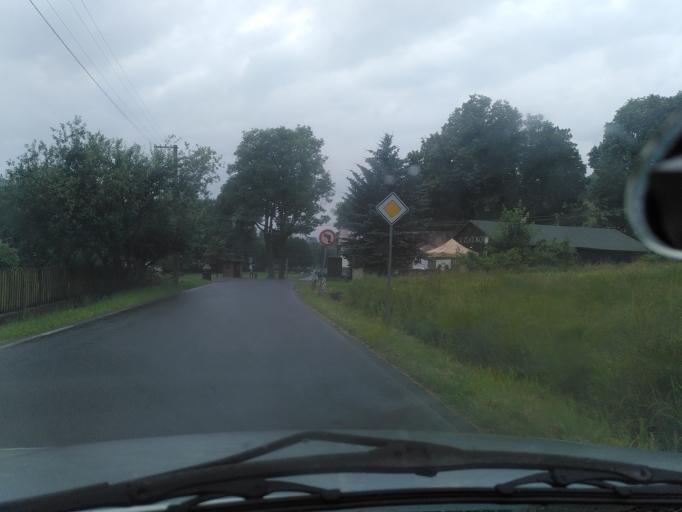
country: CZ
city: Novy Bor
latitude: 50.8157
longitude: 14.5324
